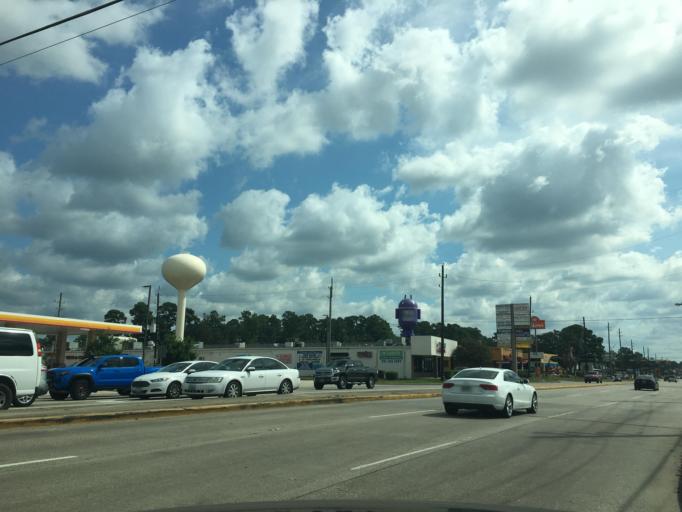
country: US
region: Texas
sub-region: Montgomery County
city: Oak Ridge North
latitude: 30.1267
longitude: -95.4425
